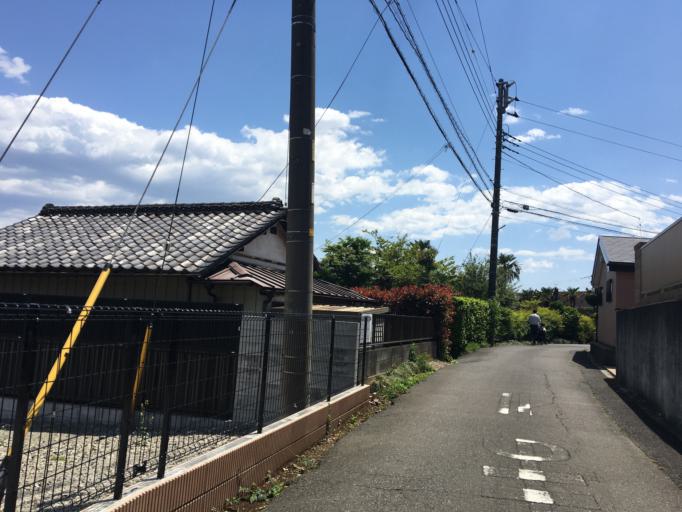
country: JP
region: Saitama
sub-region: Kawaguchi-shi
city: Hatogaya-honcho
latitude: 35.8476
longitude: 139.7483
